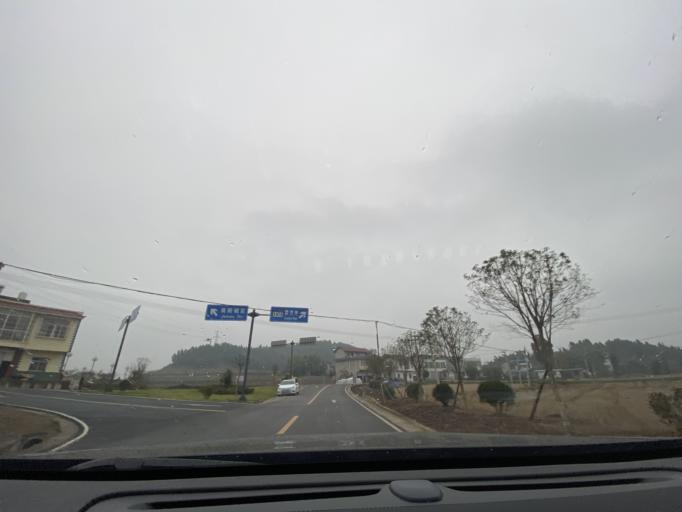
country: CN
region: Sichuan
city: Jiancheng
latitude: 30.3955
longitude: 104.6325
